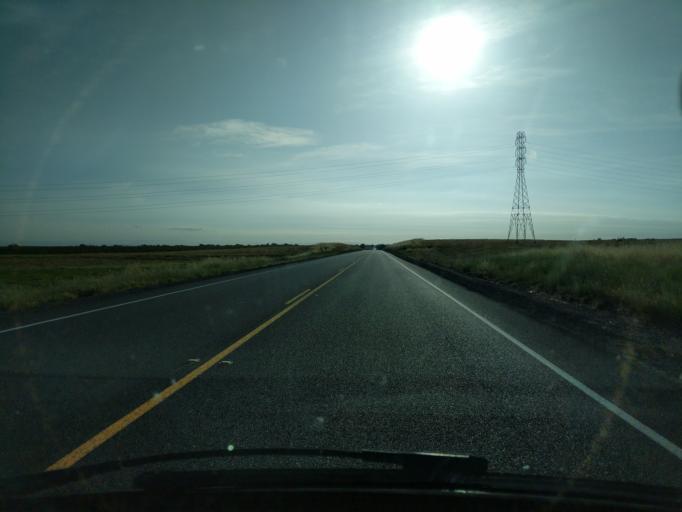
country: US
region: California
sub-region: San Joaquin County
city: Escalon
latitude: 37.9302
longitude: -120.9554
